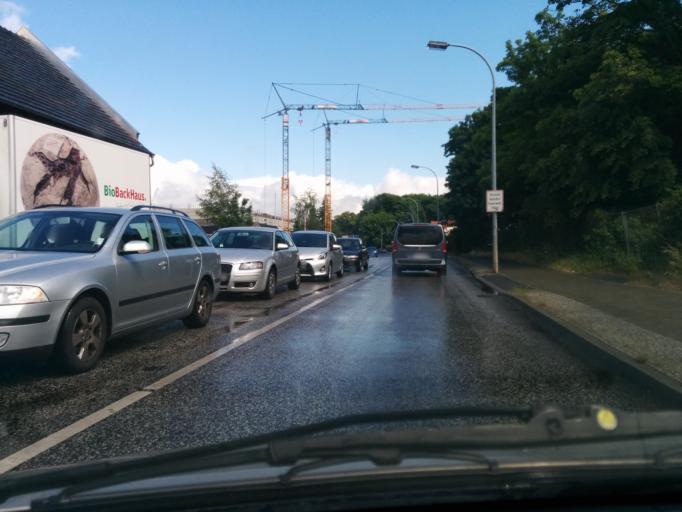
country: DE
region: Brandenburg
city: Falkensee
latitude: 52.5672
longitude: 13.1034
